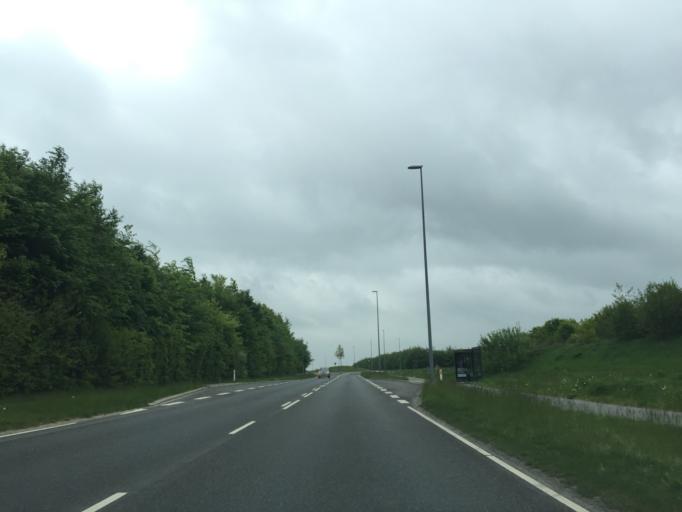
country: DK
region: Central Jutland
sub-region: Silkeborg Kommune
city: Svejbaek
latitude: 56.1923
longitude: 9.6072
